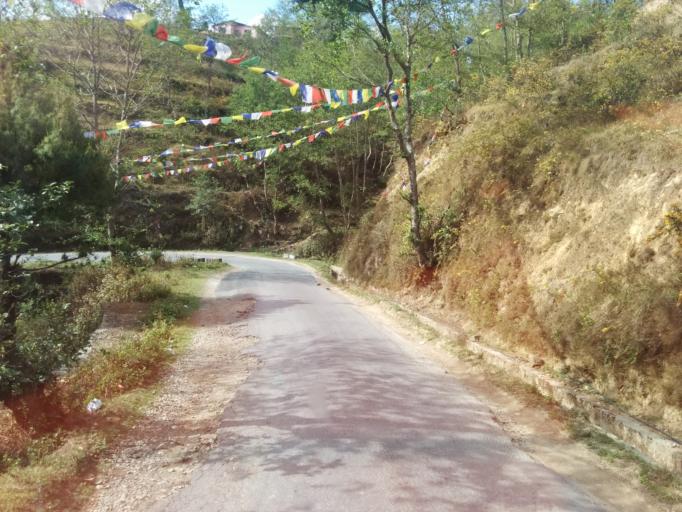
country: NP
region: Central Region
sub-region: Bagmati Zone
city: Nagarkot
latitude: 27.7096
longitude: 85.5021
